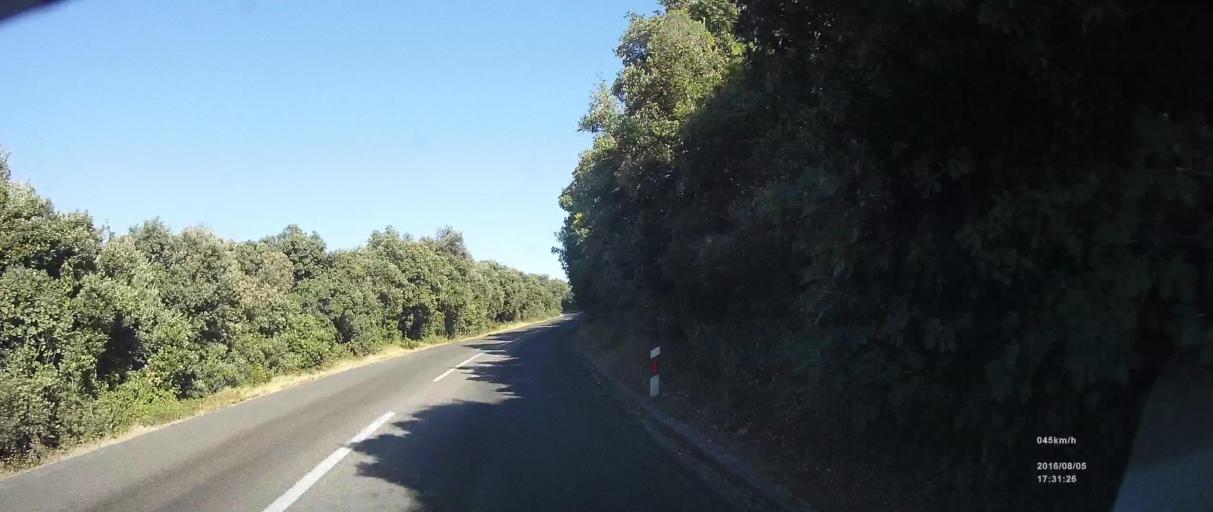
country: HR
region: Dubrovacko-Neretvanska
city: Blato
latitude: 42.7736
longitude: 17.4203
